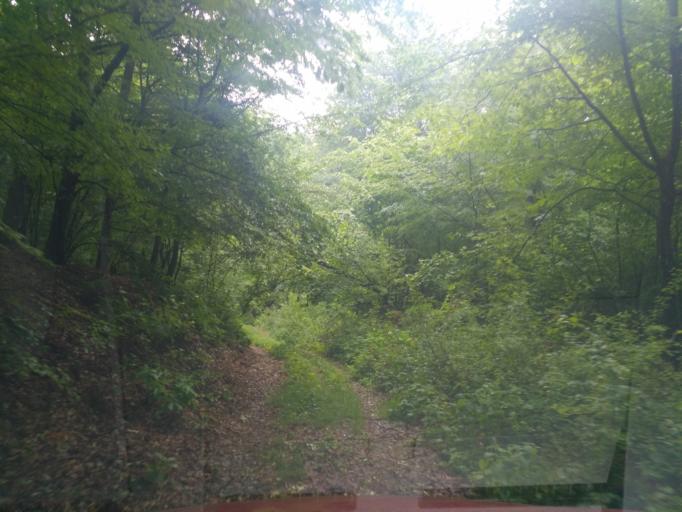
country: SK
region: Kosicky
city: Moldava nad Bodvou
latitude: 48.6951
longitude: 21.0756
